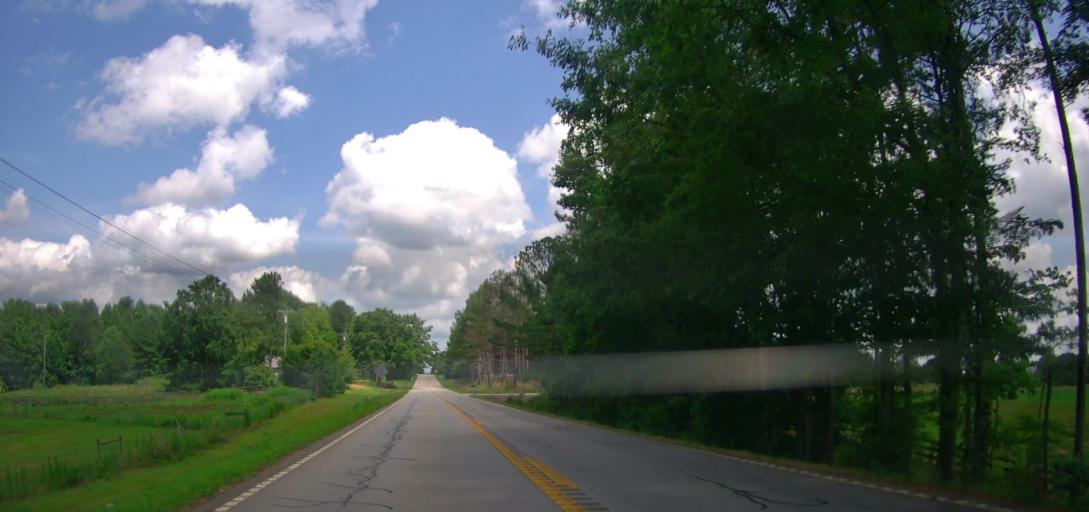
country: US
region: Georgia
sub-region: Heard County
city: Franklin
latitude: 33.3551
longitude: -85.2119
